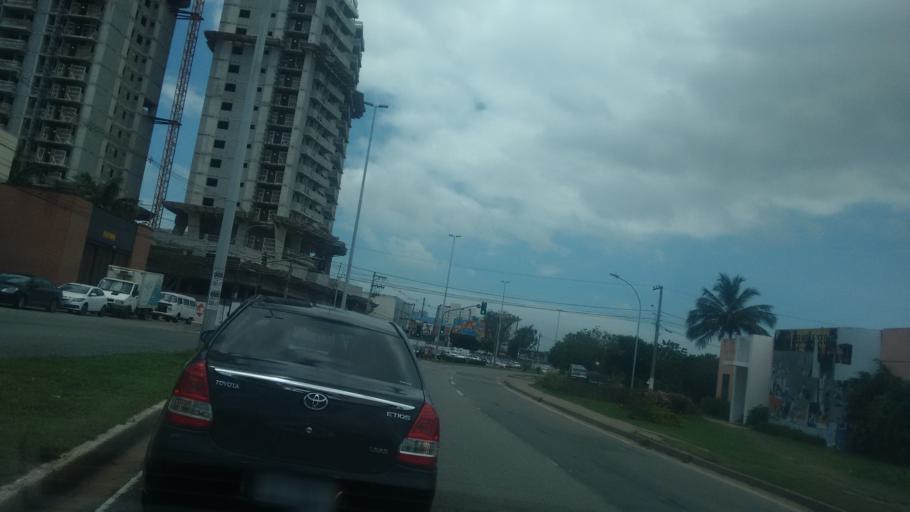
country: BR
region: Espirito Santo
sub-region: Vila Velha
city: Vila Velha
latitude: -20.2509
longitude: -40.2726
